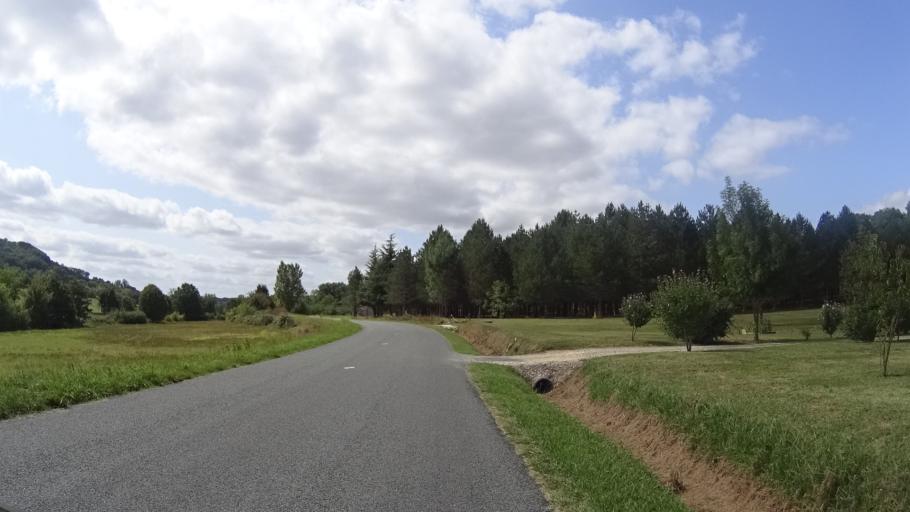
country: FR
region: Aquitaine
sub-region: Departement du Lot-et-Garonne
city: Pont-du-Casse
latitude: 44.2529
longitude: 0.6903
